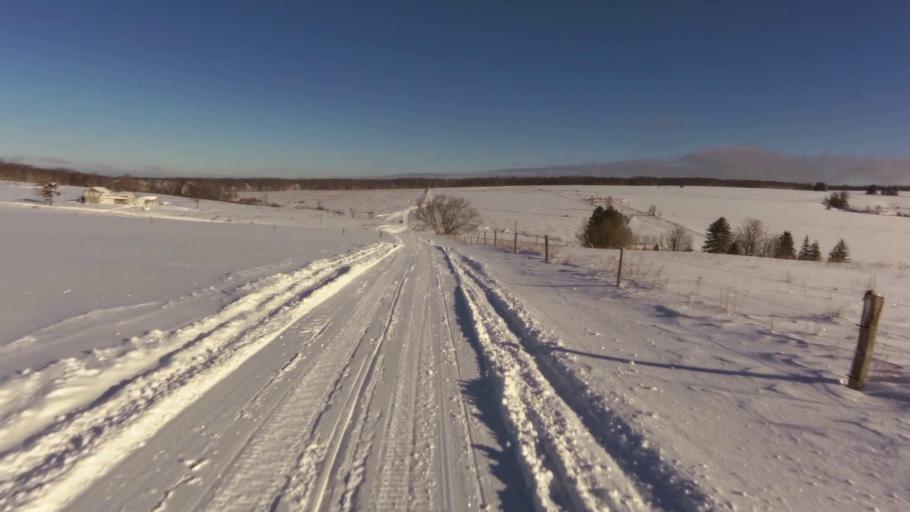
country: US
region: New York
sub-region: Chautauqua County
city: Falconer
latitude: 42.2590
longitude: -79.2029
